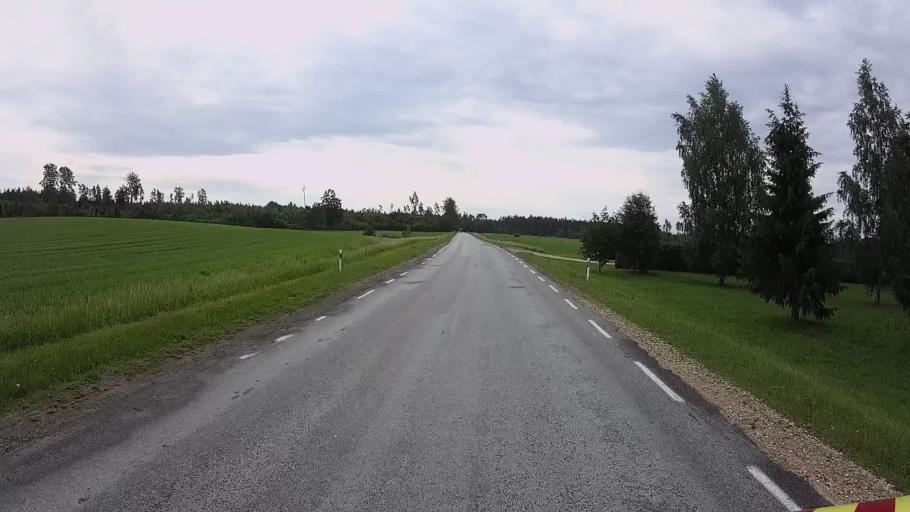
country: EE
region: Viljandimaa
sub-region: Karksi vald
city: Karksi-Nuia
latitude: 58.2289
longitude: 25.6046
